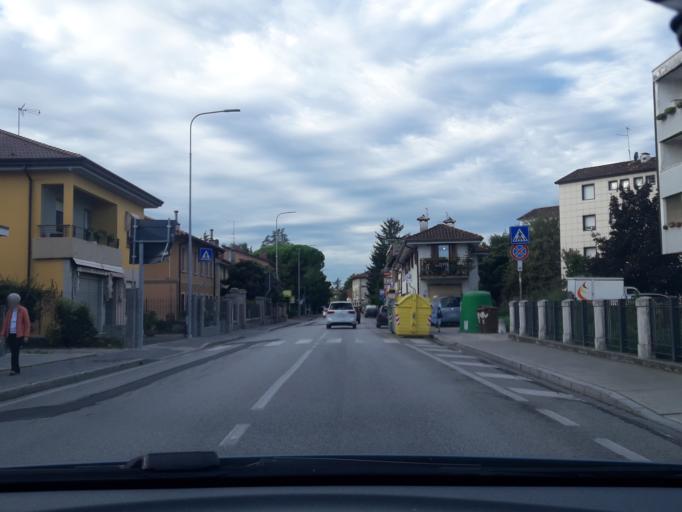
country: IT
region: Friuli Venezia Giulia
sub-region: Provincia di Udine
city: Basaldella
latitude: 46.0478
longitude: 13.2227
